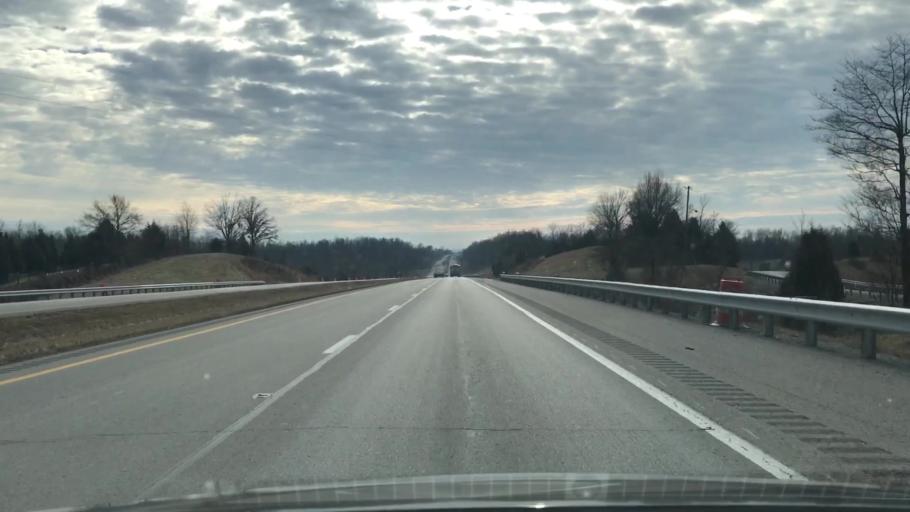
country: US
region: Kentucky
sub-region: Ohio County
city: Hartford
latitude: 37.5225
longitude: -86.9201
